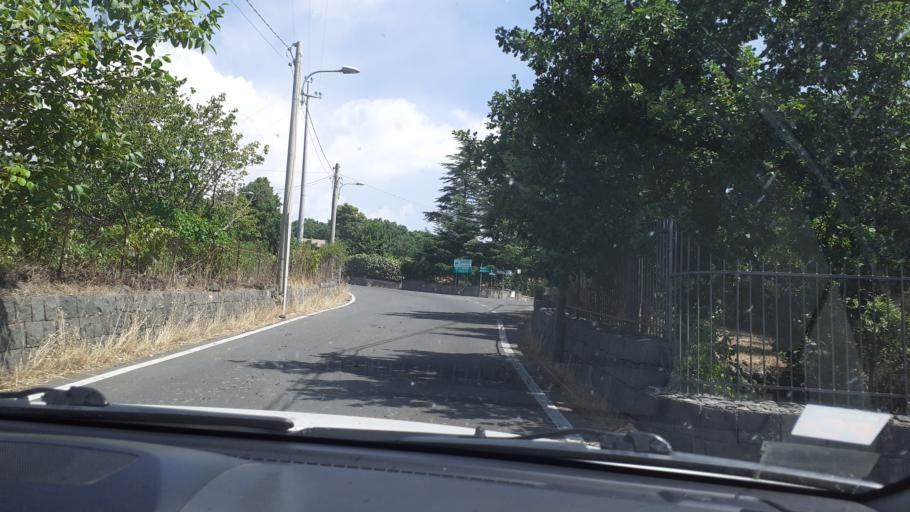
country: IT
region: Sicily
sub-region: Catania
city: Nicolosi
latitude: 37.6322
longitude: 15.0247
